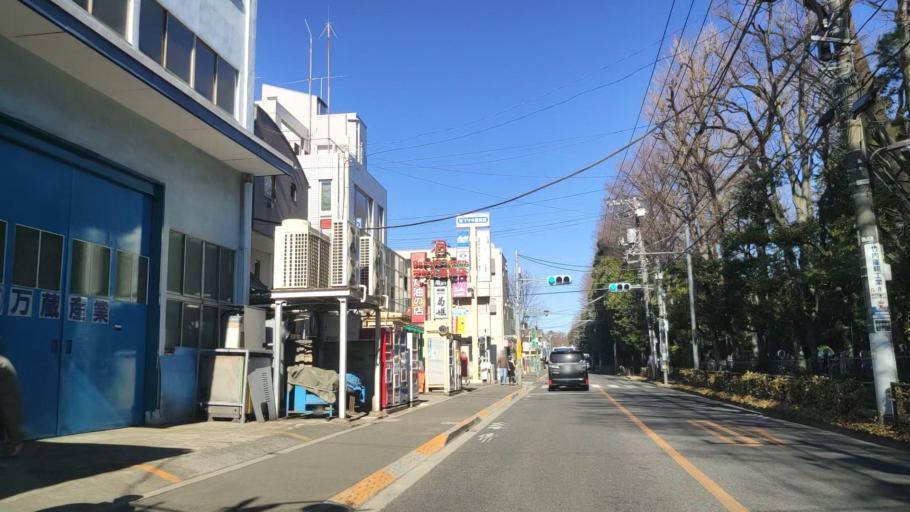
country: JP
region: Tokyo
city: Kamirenjaku
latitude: 35.6958
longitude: 139.5699
